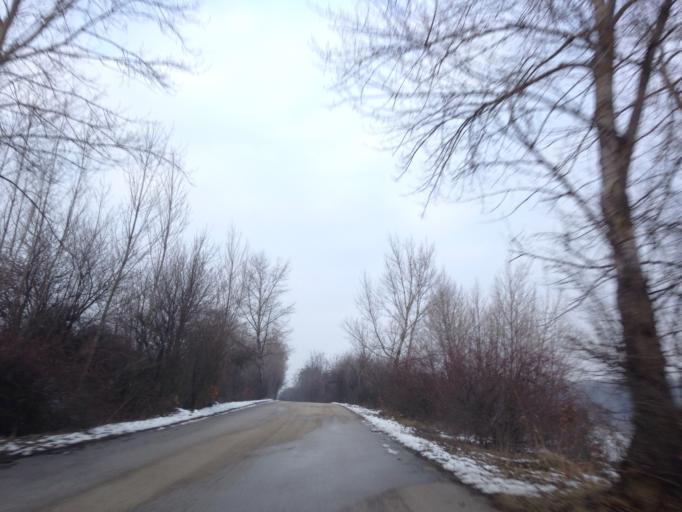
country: SK
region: Nitriansky
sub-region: Okres Nitra
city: Vrable
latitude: 48.0855
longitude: 18.3704
